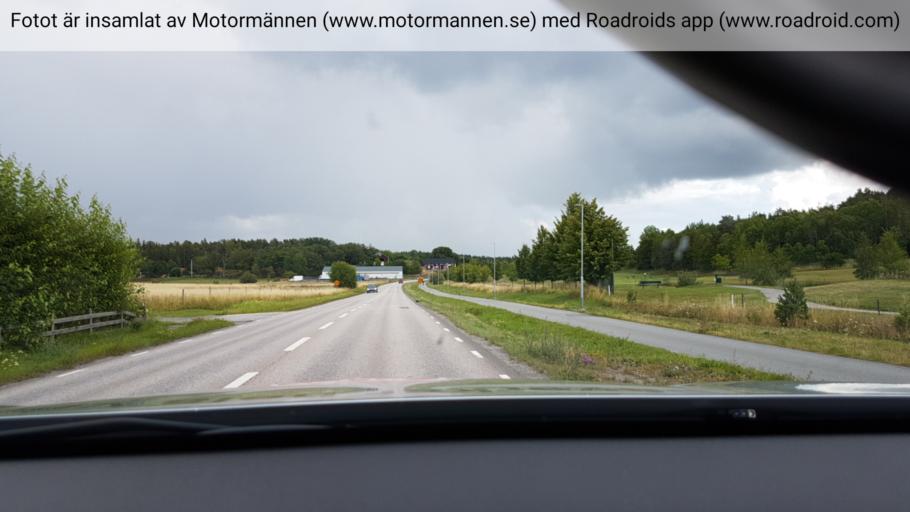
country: SE
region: Stockholm
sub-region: Ekero Kommun
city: Ekeroe
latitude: 59.3210
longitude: 17.7645
